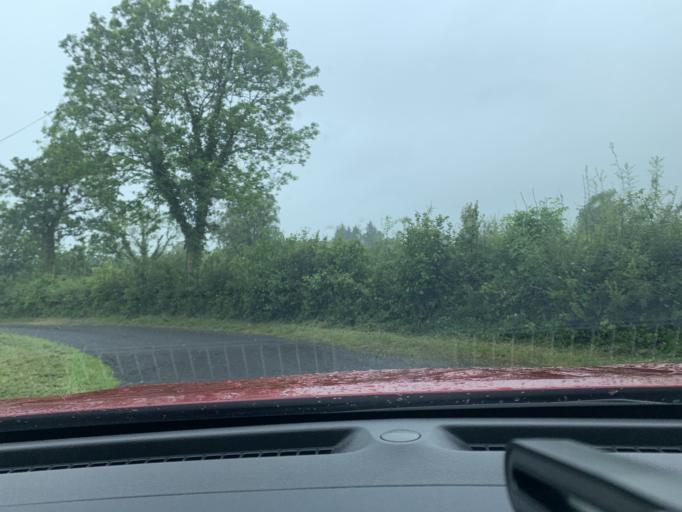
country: GB
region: Northern Ireland
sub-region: Fermanagh District
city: Enniskillen
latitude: 54.2664
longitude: -7.7403
